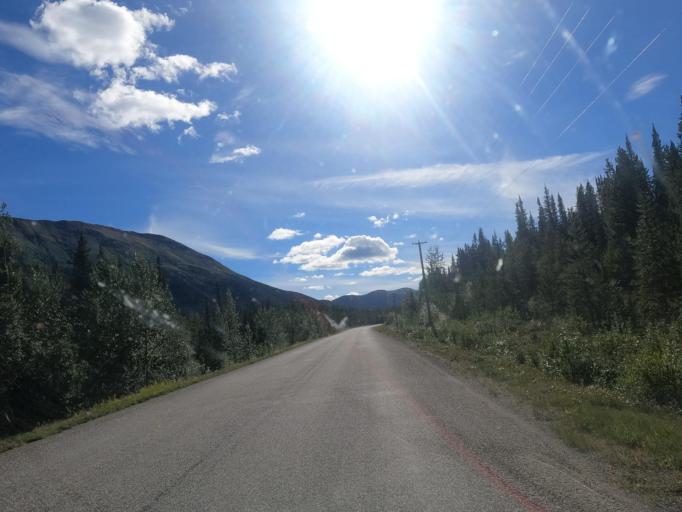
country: CA
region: Yukon
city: Watson Lake
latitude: 59.2793
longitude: -129.5490
